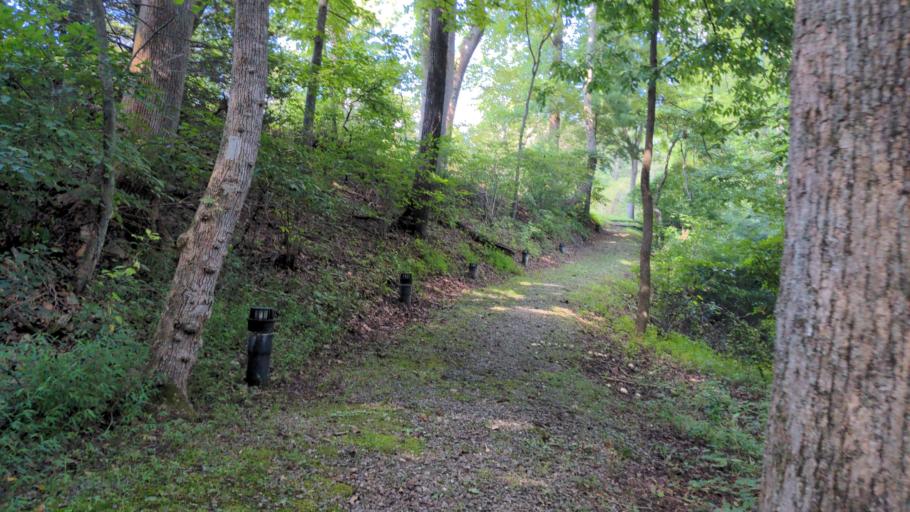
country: US
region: Virginia
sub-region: Henry County
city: Bassett
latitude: 36.7928
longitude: -80.1158
